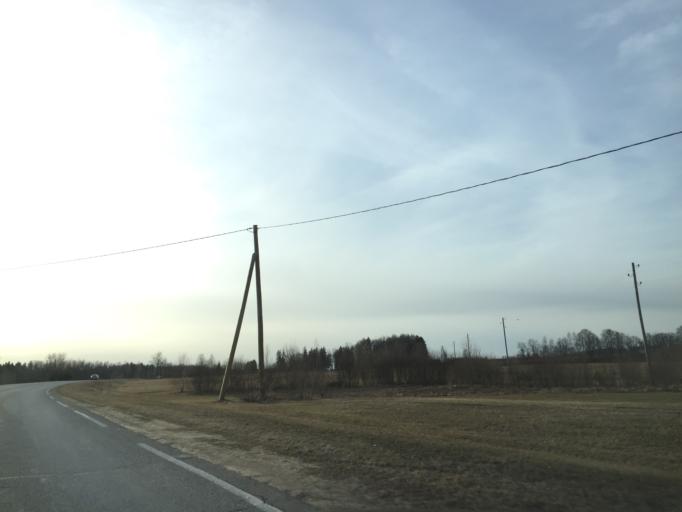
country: LV
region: Krimulda
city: Ragana
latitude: 57.1642
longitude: 24.7565
